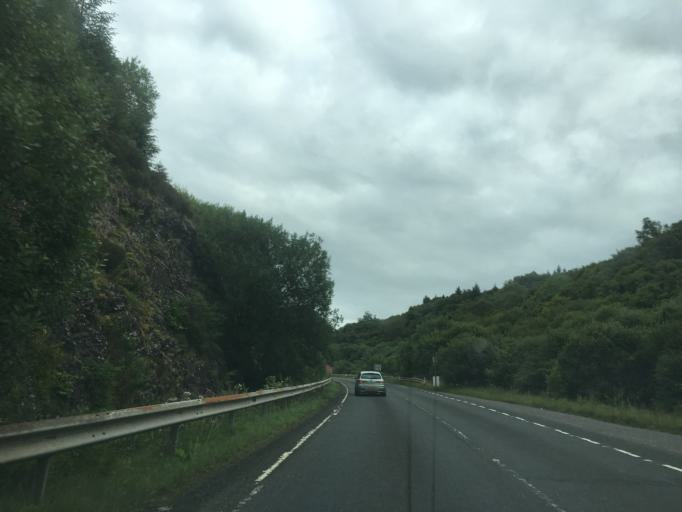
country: GB
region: Scotland
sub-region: Argyll and Bute
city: Oban
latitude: 56.3107
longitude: -5.4695
